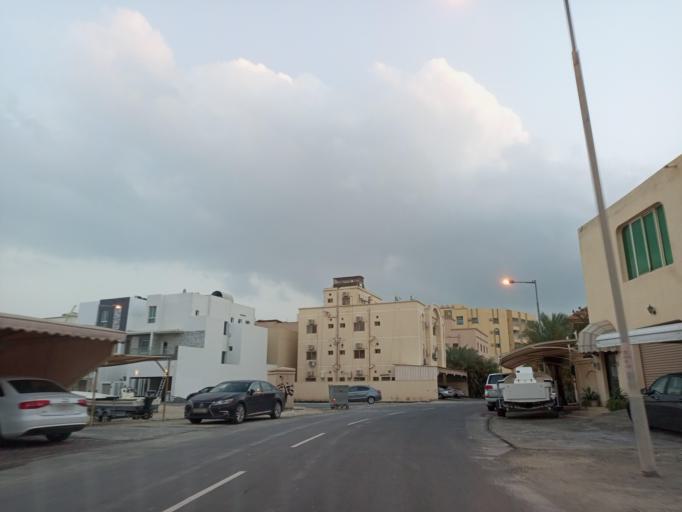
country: BH
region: Muharraq
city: Al Hadd
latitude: 26.2318
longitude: 50.6551
